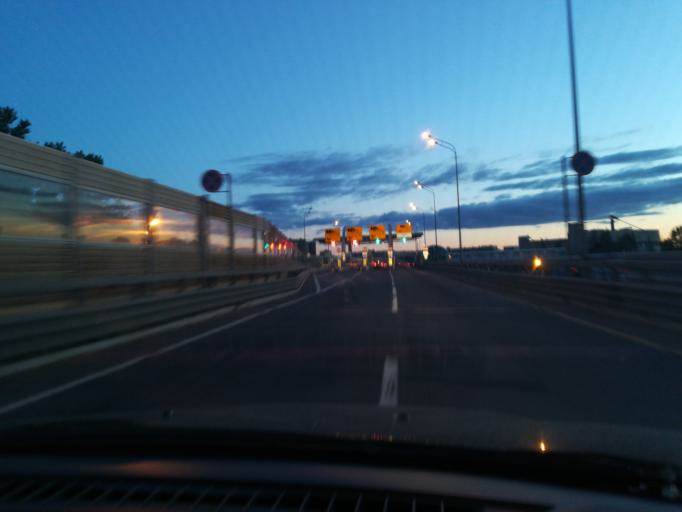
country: RU
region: St.-Petersburg
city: Avtovo
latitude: 59.8556
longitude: 30.2778
